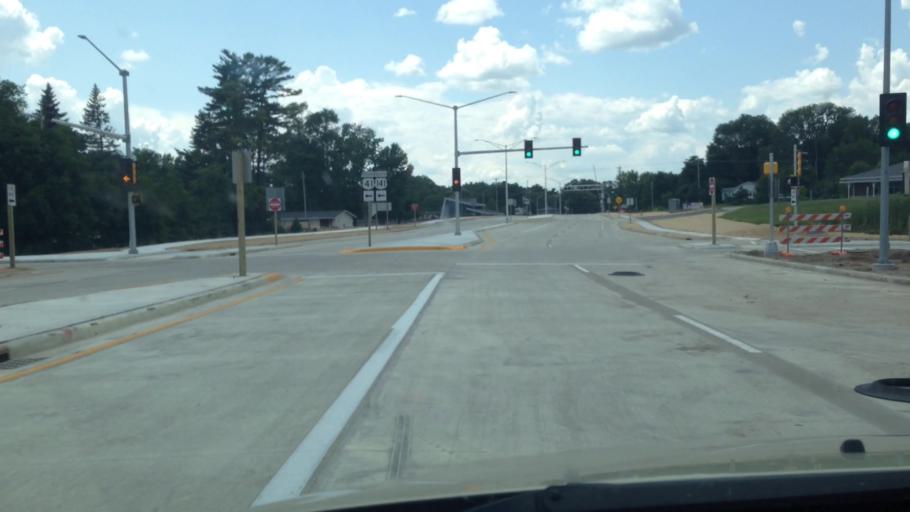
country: US
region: Wisconsin
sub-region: Brown County
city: Suamico
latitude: 44.6351
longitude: -88.0469
